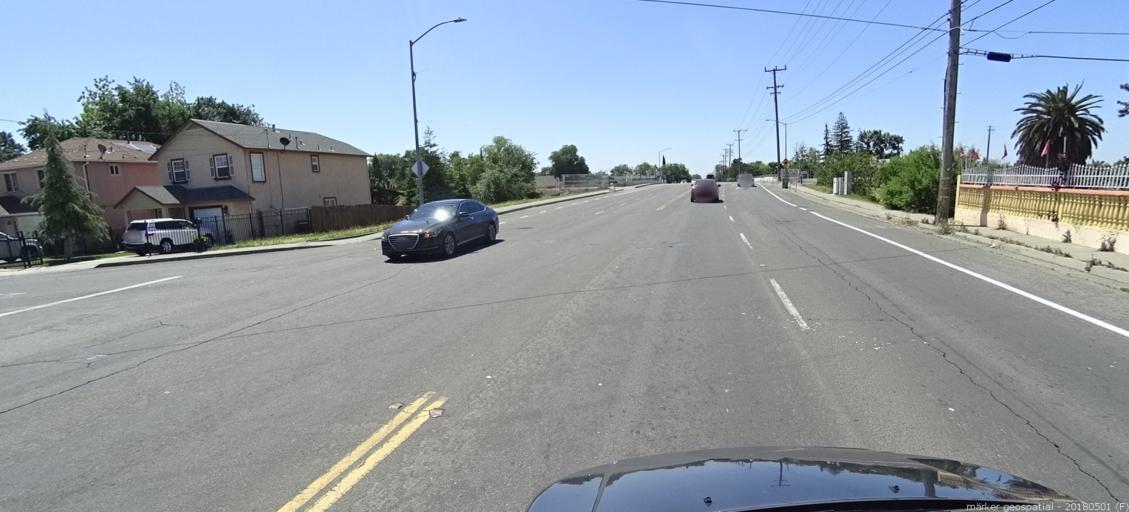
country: US
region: California
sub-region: Sacramento County
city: Rio Linda
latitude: 38.6270
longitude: -121.4462
